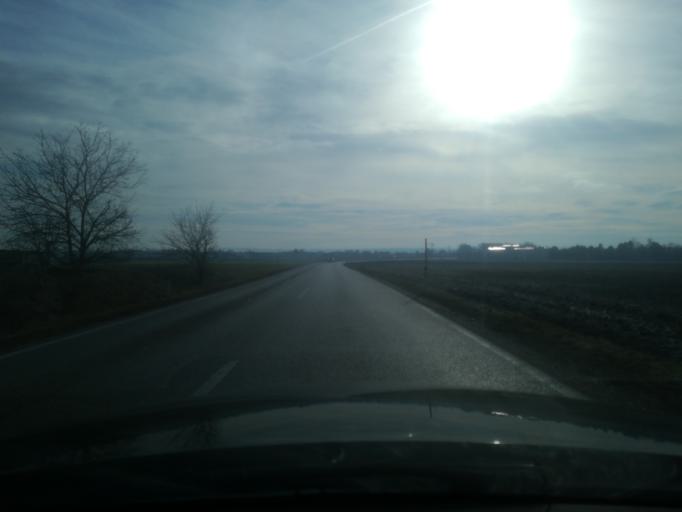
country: AT
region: Upper Austria
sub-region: Wels-Land
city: Marchtrenk
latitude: 48.2022
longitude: 14.1087
